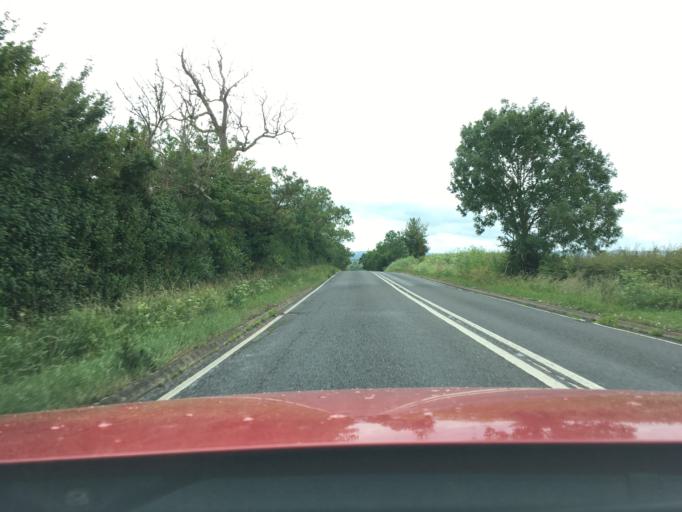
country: GB
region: England
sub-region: Warwickshire
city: Shipston on Stour
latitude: 52.1193
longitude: -1.6098
